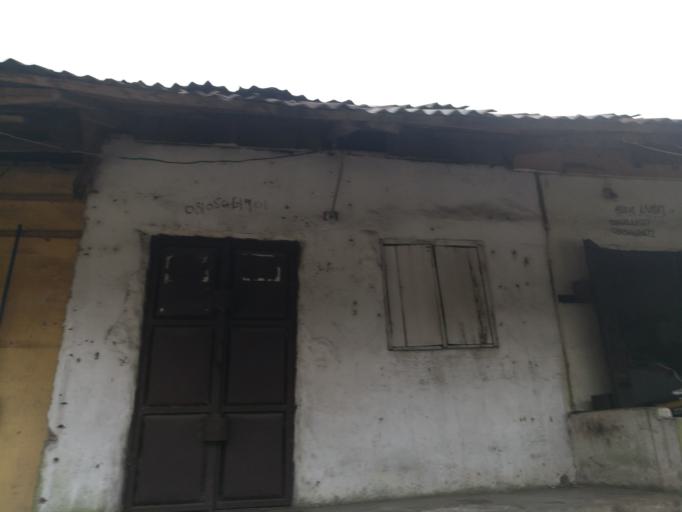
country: NG
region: Rivers
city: Okrika
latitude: 4.7890
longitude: 7.1268
